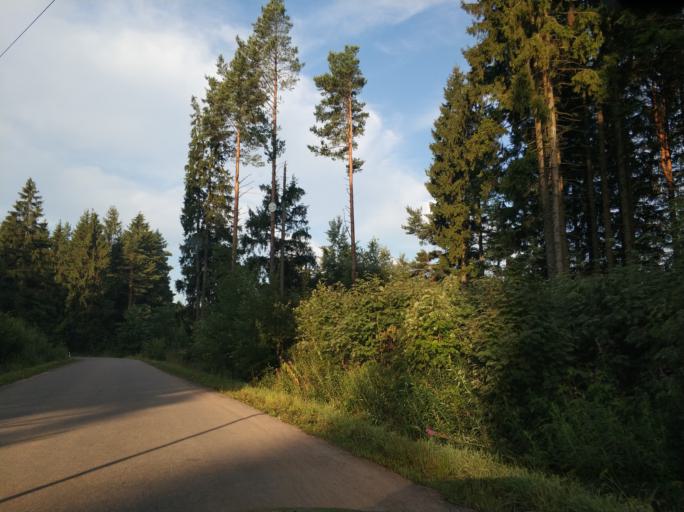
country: RU
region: Leningrad
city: Shcheglovo
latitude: 60.0564
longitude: 30.7470
